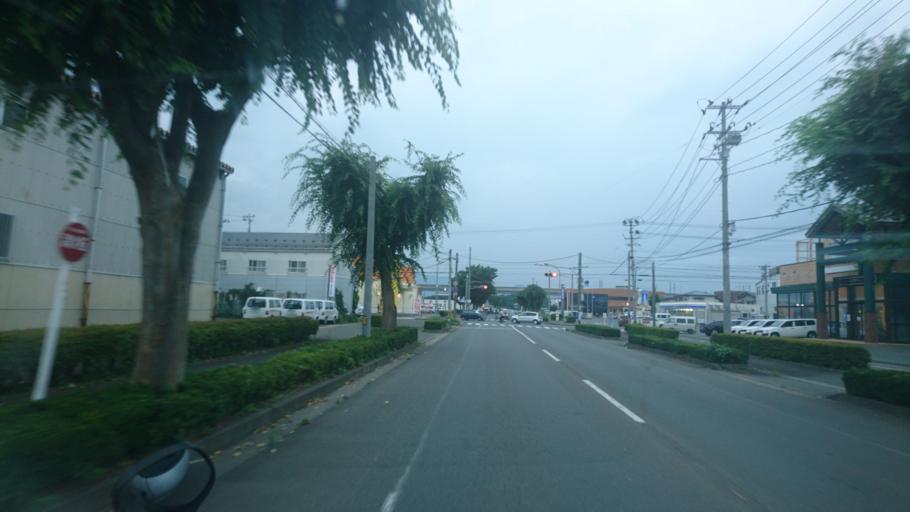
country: JP
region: Iwate
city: Morioka-shi
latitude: 39.6669
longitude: 141.1529
